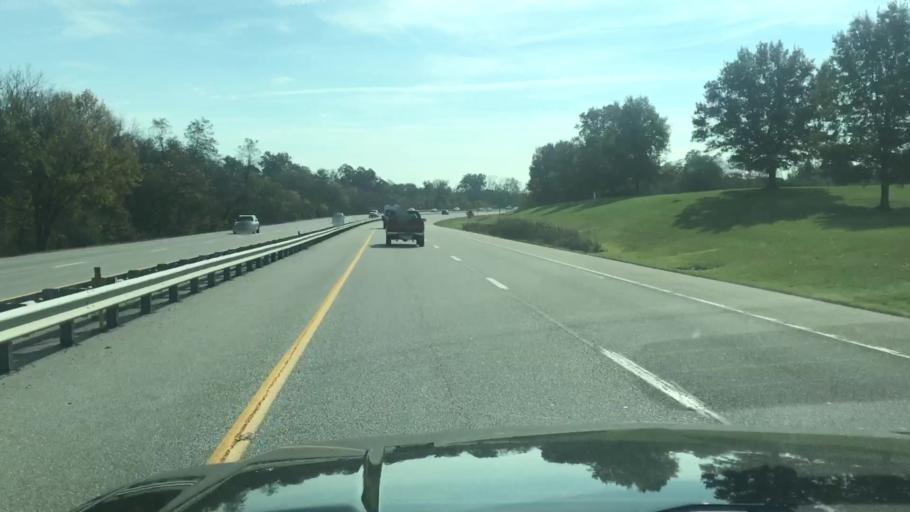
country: US
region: Pennsylvania
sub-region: Cumberland County
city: Mechanicsburg
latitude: 40.2578
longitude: -77.0348
